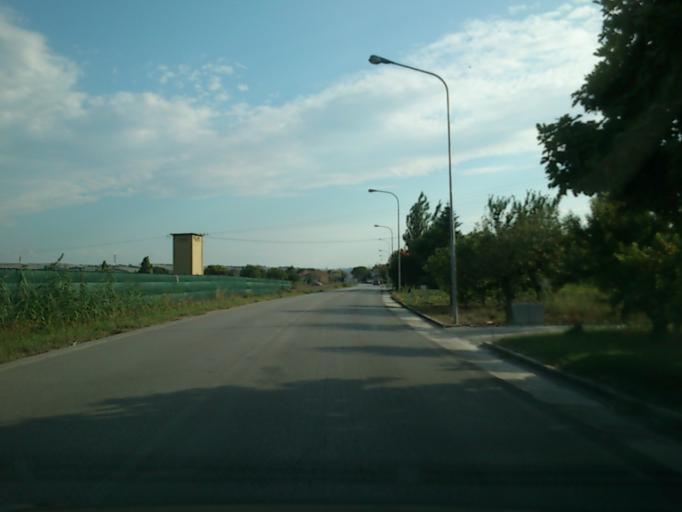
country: IT
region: The Marches
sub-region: Provincia di Pesaro e Urbino
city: Fano
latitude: 43.8232
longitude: 13.0535
